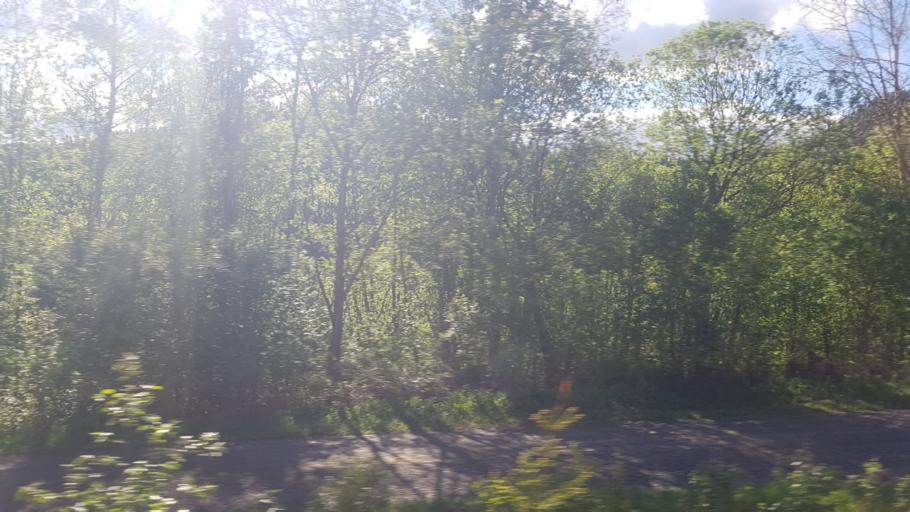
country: NO
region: Sor-Trondelag
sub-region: Midtre Gauldal
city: Storen
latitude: 62.9789
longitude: 10.2230
